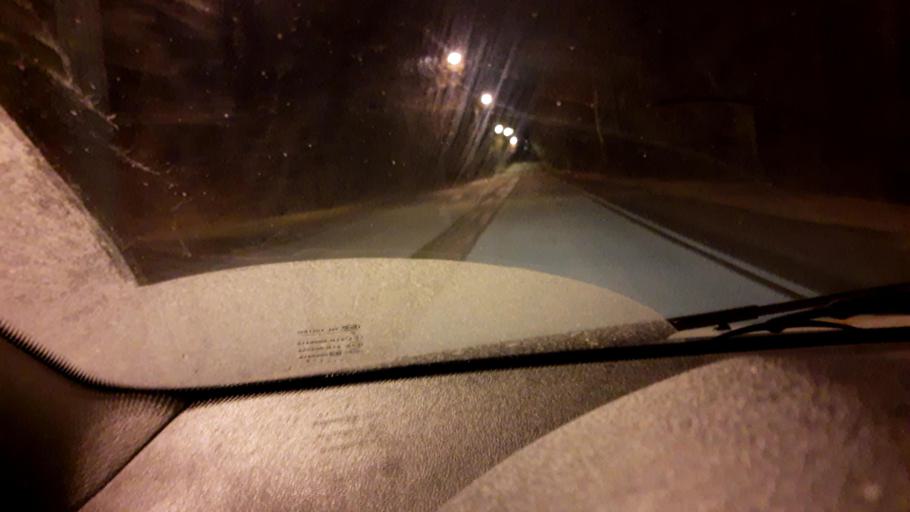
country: RU
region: Bashkortostan
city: Ufa
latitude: 54.8587
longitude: 56.0757
